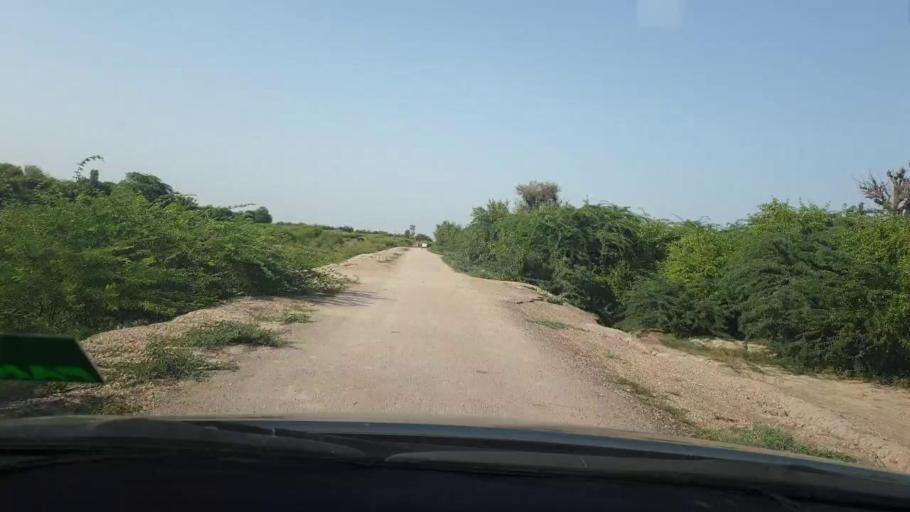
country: PK
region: Sindh
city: Naukot
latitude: 24.8703
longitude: 69.3171
